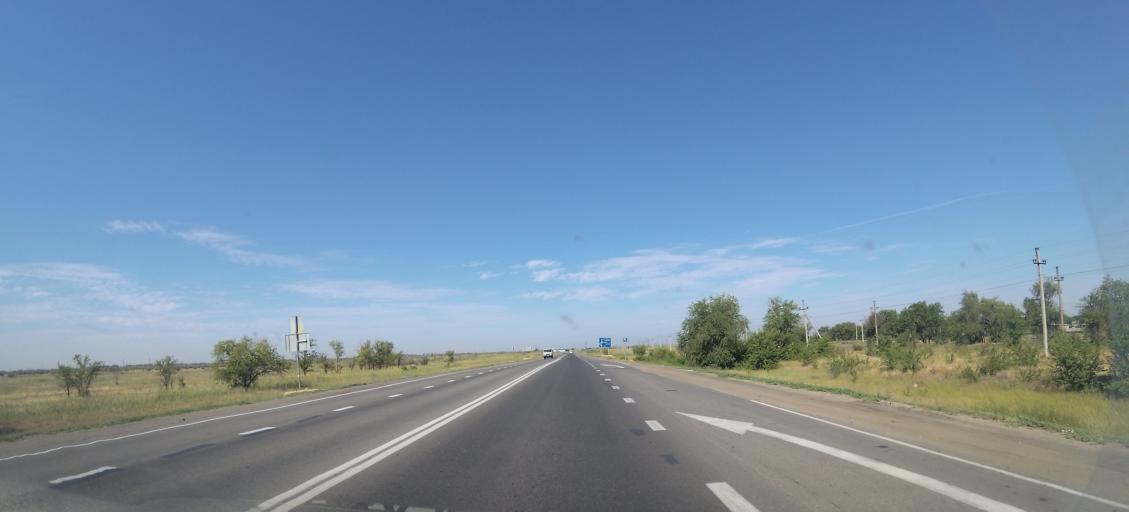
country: RU
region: Volgograd
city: Oktyabr'skiy
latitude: 48.6795
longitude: 43.9044
